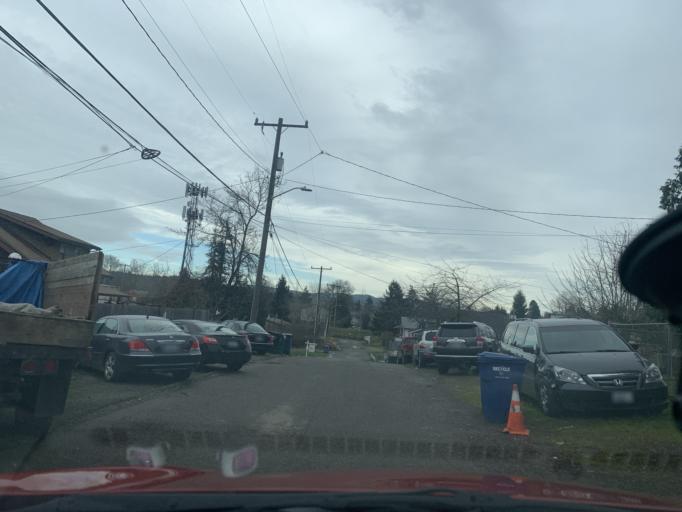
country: US
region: Washington
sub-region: King County
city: Bryn Mawr-Skyway
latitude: 47.5219
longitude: -122.2693
